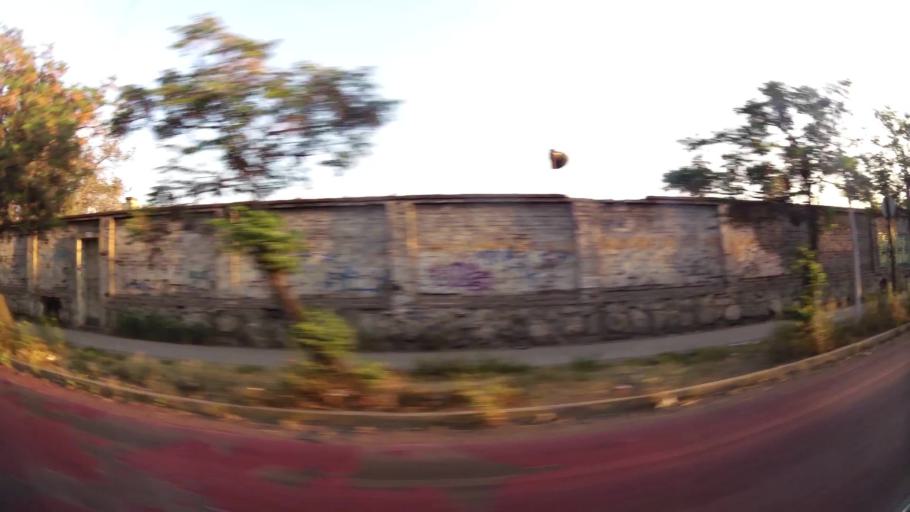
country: CL
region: Santiago Metropolitan
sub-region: Provincia de Santiago
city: Santiago
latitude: -33.4707
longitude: -70.6747
